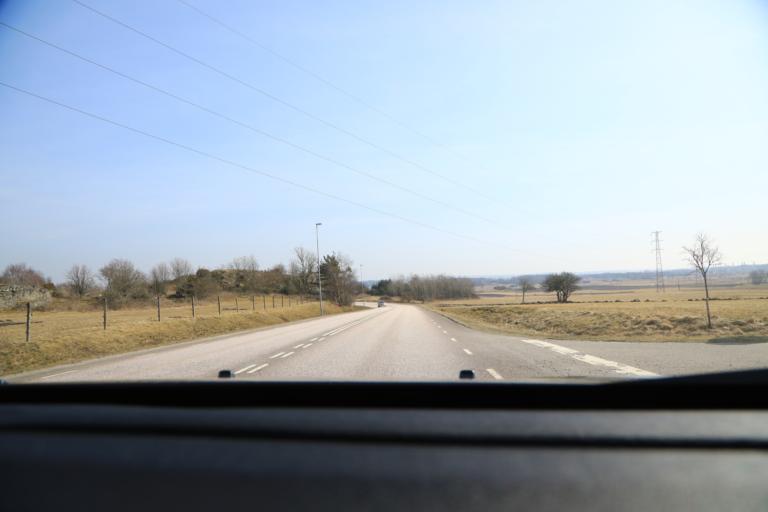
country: SE
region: Halland
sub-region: Kungsbacka Kommun
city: Frillesas
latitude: 57.2546
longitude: 12.1575
